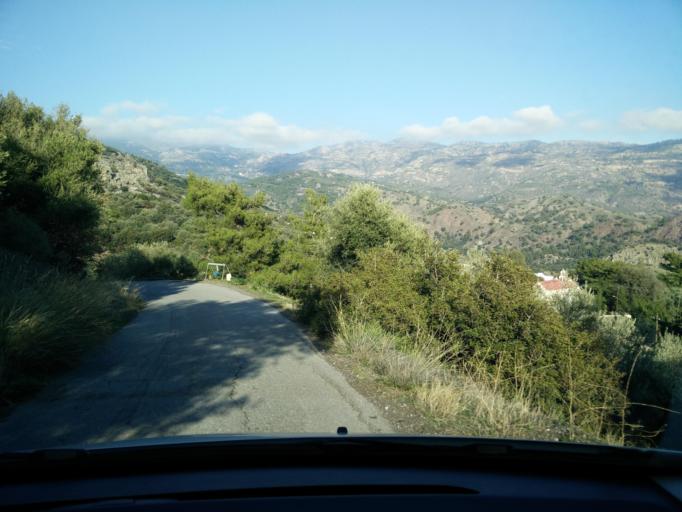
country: GR
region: Crete
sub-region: Nomos Lasithiou
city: Gra Liyia
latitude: 35.0358
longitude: 25.5714
